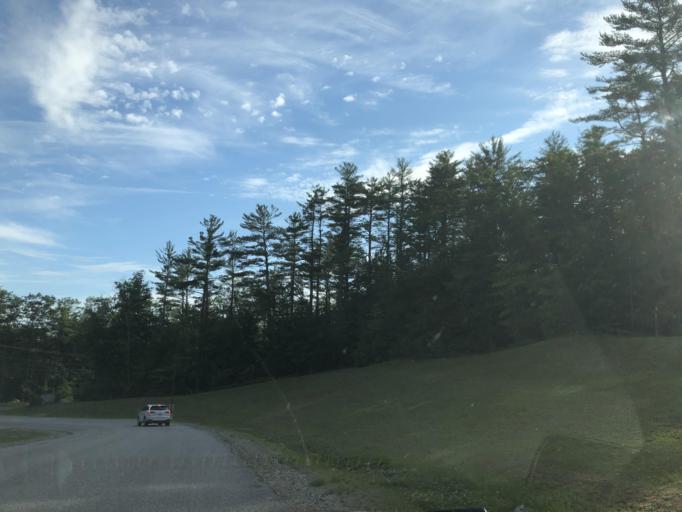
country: US
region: New Hampshire
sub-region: Merrimack County
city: Sutton
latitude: 43.3468
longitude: -71.9329
